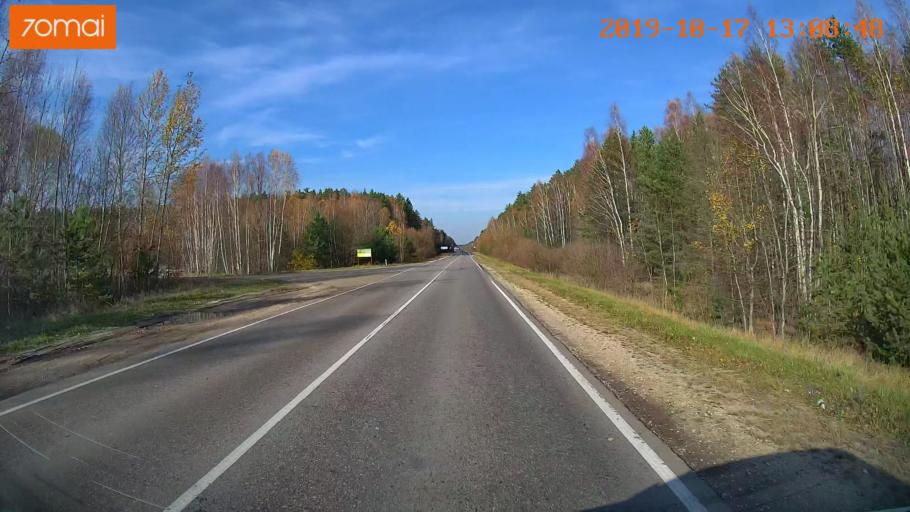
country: RU
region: Rjazan
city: Syntul
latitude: 54.9942
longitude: 41.2670
